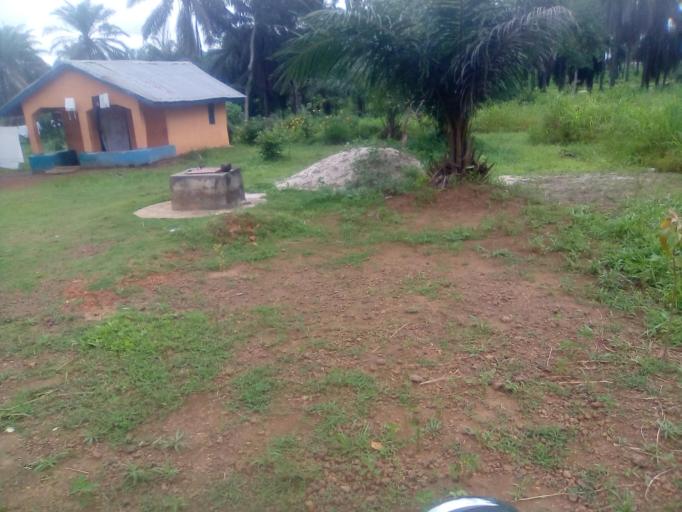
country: SL
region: Southern Province
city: Moyamba
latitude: 8.1472
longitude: -12.4347
